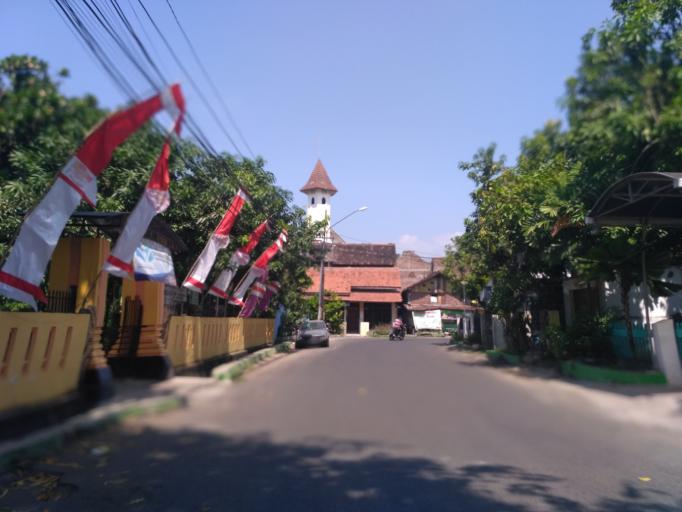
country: ID
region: Central Java
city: Semarang
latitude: -6.9967
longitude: 110.4229
